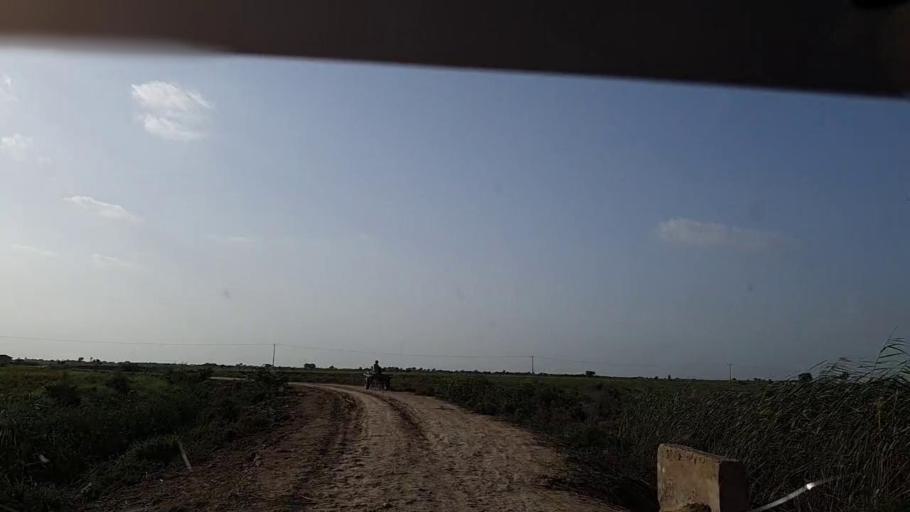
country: PK
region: Sindh
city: Badin
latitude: 24.5601
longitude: 68.8860
